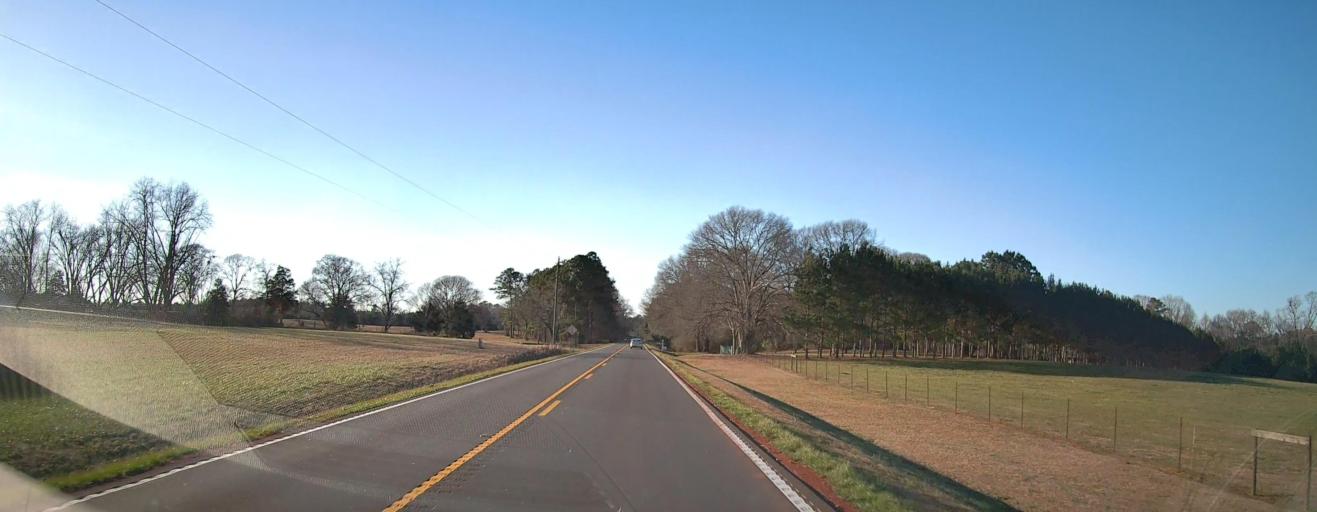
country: US
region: Georgia
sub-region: Meriwether County
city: Manchester
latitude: 32.9069
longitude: -84.7225
